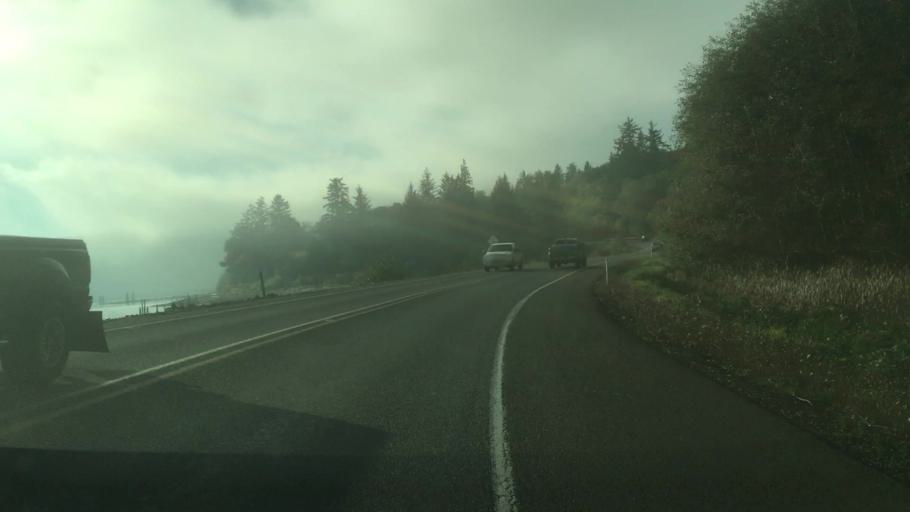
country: US
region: Oregon
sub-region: Clatsop County
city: Astoria
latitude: 46.2698
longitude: -123.8204
